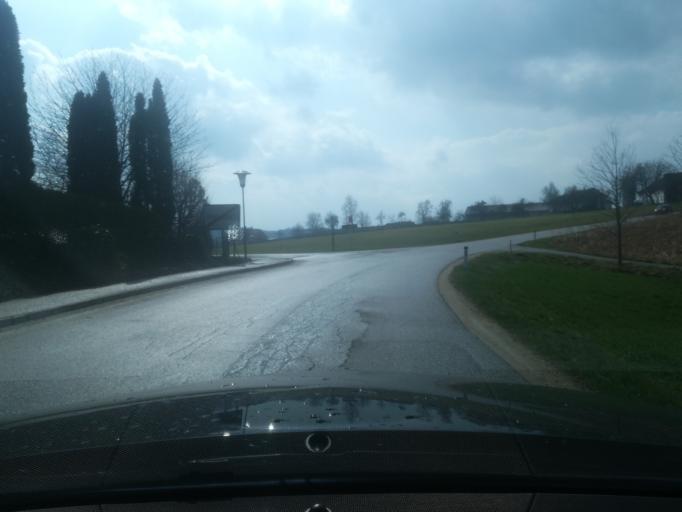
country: AT
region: Upper Austria
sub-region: Politischer Bezirk Perg
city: Perg
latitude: 48.3191
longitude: 14.6247
